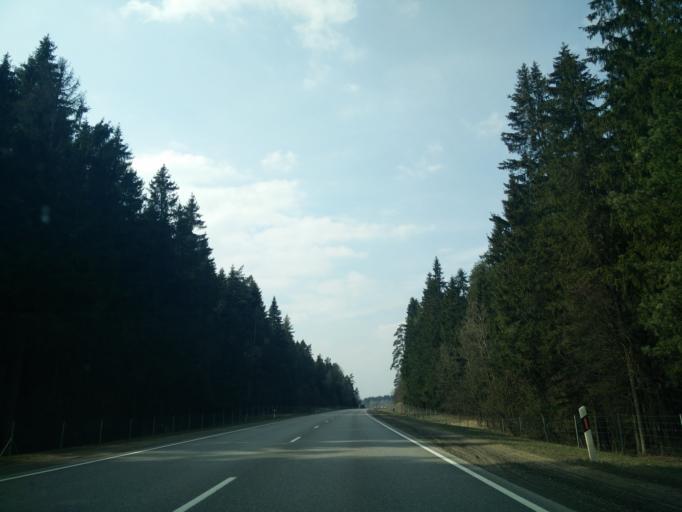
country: LT
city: Lentvaris
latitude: 54.6192
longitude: 25.0820
